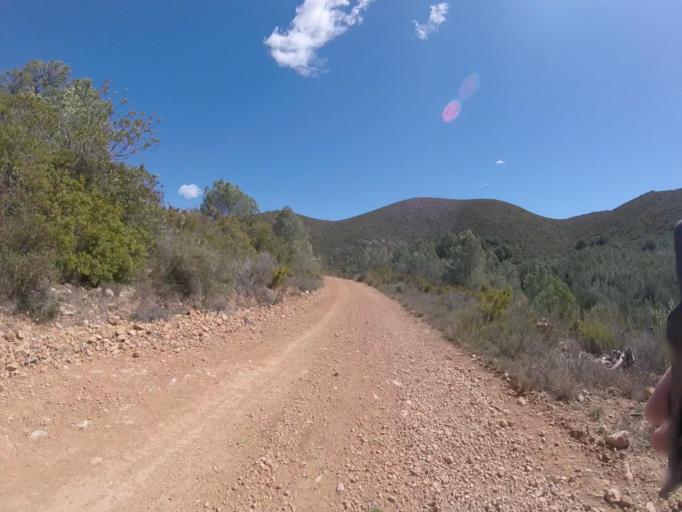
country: ES
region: Valencia
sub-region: Provincia de Castello
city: Cabanes
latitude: 40.1612
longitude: 0.1124
